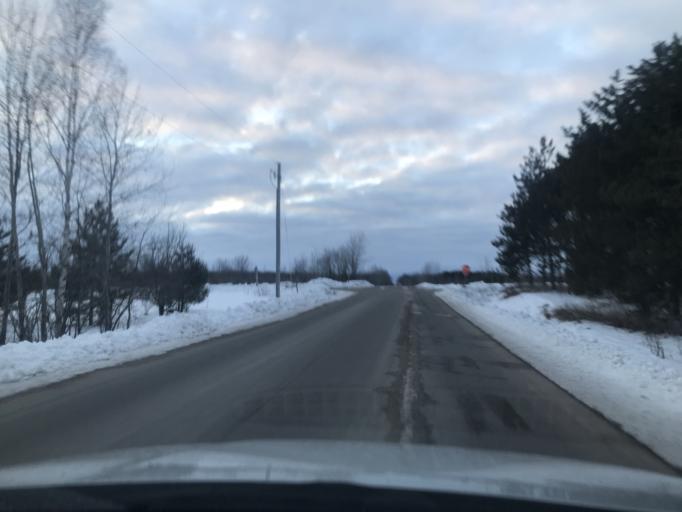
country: US
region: Wisconsin
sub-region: Marinette County
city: Peshtigo
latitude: 45.1647
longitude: -87.7585
